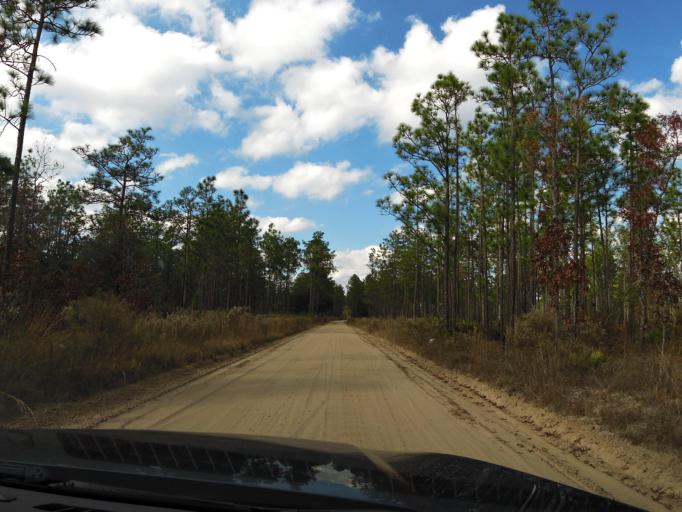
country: US
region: Florida
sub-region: Clay County
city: Middleburg
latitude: 30.1149
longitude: -81.9225
